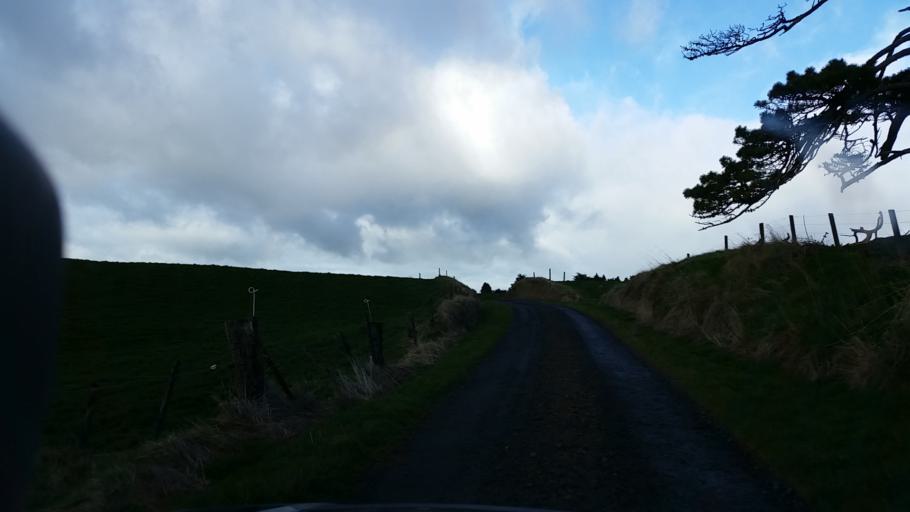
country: NZ
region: Taranaki
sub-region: South Taranaki District
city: Eltham
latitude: -39.3305
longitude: 174.1726
